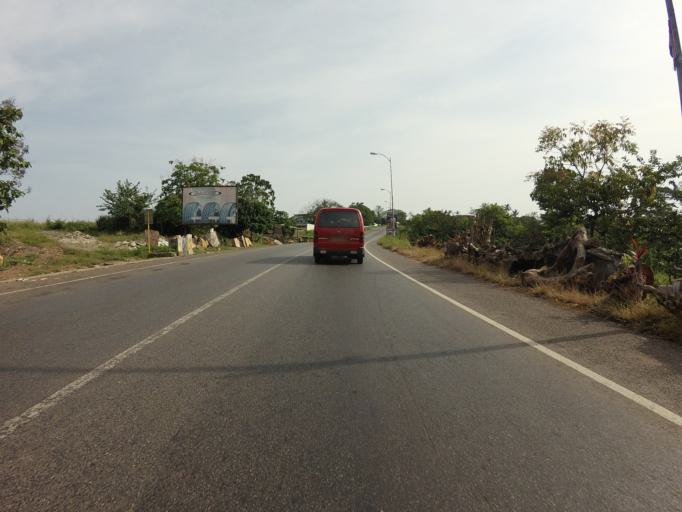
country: GH
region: Eastern
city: Aburi
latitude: 5.8340
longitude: -0.1822
